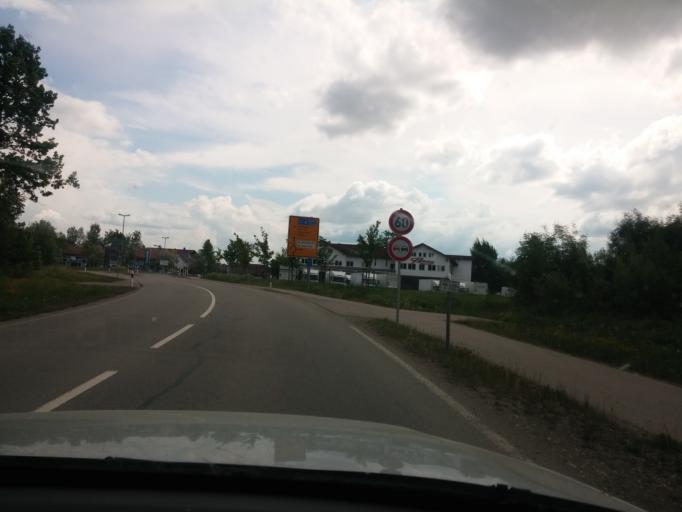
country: DE
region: Bavaria
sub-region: Upper Bavaria
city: Holzkirchen
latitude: 47.8824
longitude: 11.7175
